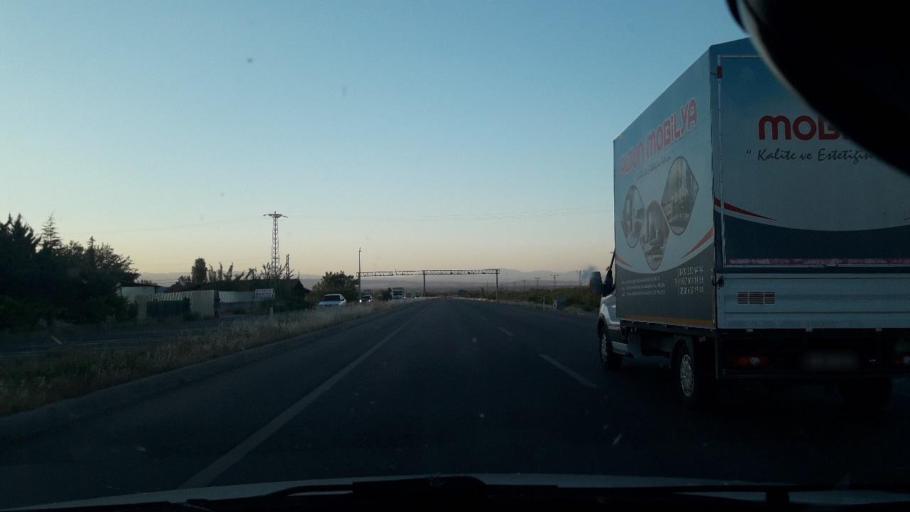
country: TR
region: Malatya
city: Malatya
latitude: 38.4486
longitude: 38.2270
